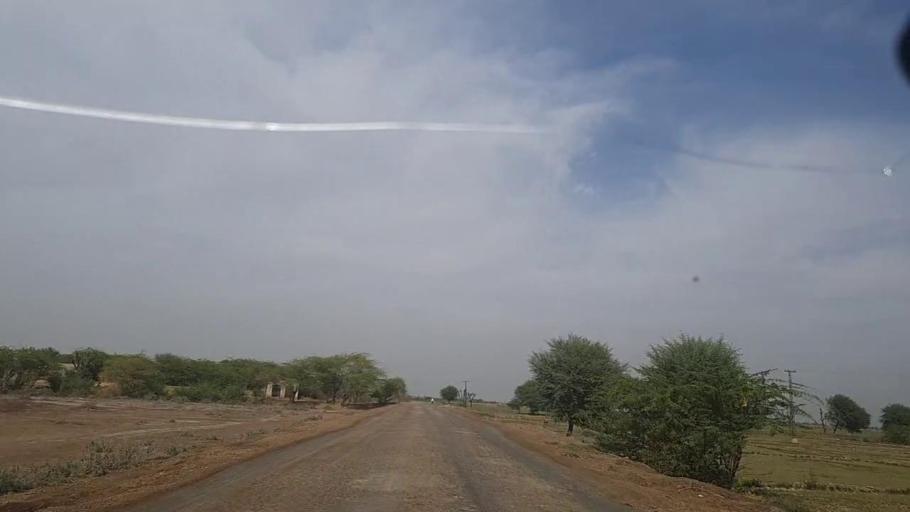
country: PK
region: Sindh
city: Pithoro
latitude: 25.5493
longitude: 69.3614
